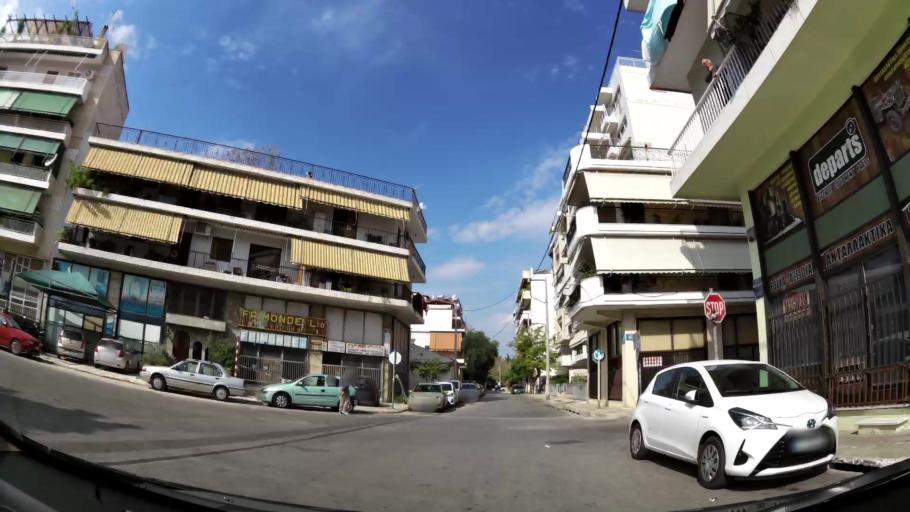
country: GR
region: Attica
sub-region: Nomarchia Athinas
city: Athens
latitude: 37.9895
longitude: 23.7089
